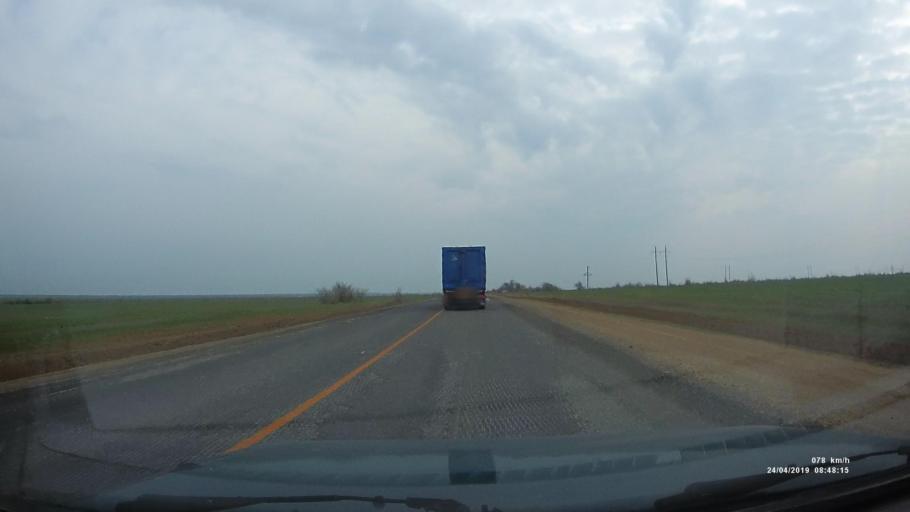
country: RU
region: Kalmykiya
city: Arshan'
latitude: 46.2500
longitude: 44.1062
